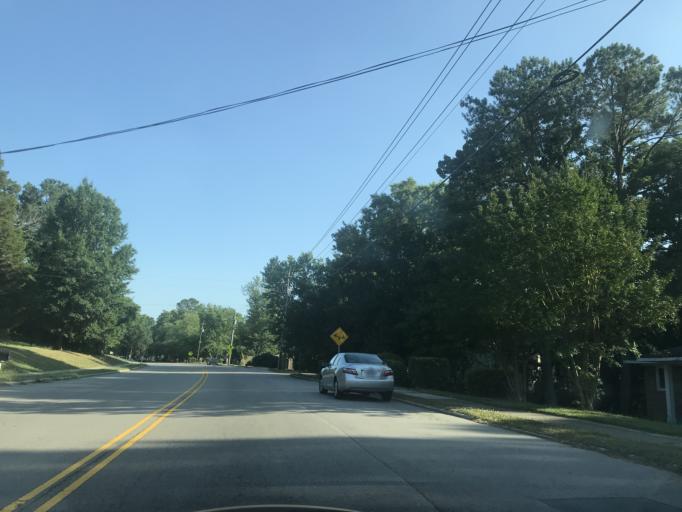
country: US
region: North Carolina
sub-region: Wake County
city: Garner
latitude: 35.7445
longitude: -78.6140
